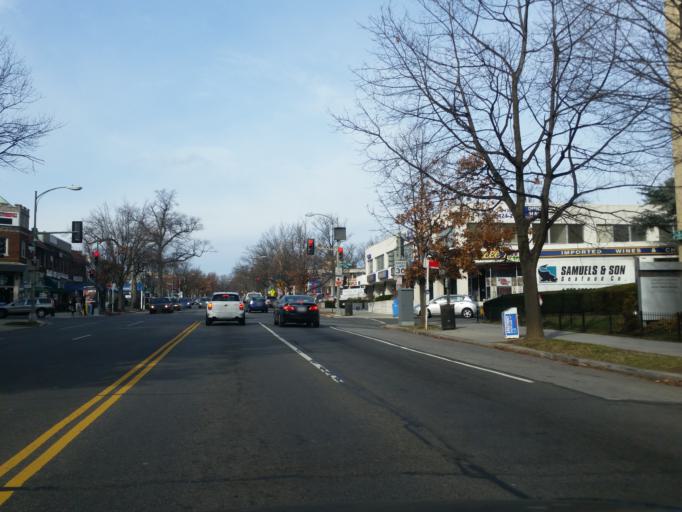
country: US
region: Maryland
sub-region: Montgomery County
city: Chevy Chase Village
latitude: 38.9627
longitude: -77.0743
